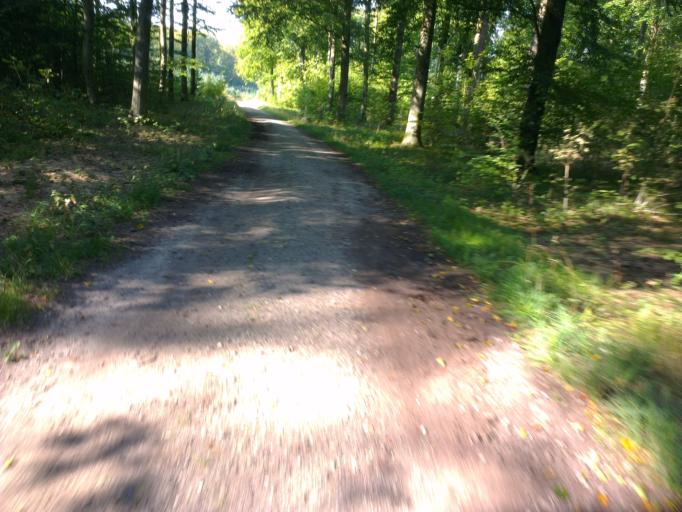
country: DK
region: Capital Region
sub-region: Frederikssund Kommune
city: Frederikssund
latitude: 55.8463
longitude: 12.0219
